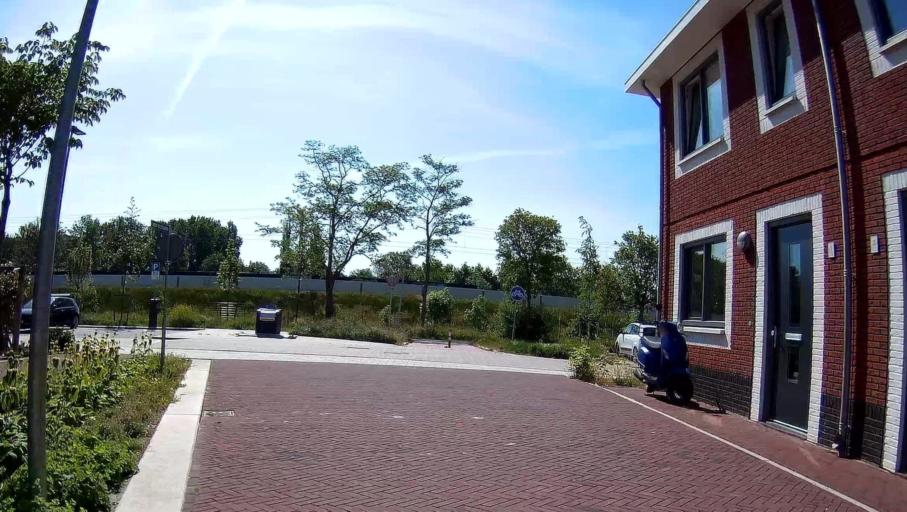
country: NL
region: South Holland
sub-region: Gemeente Schiedam
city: Schiedam
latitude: 51.9192
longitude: 4.3739
